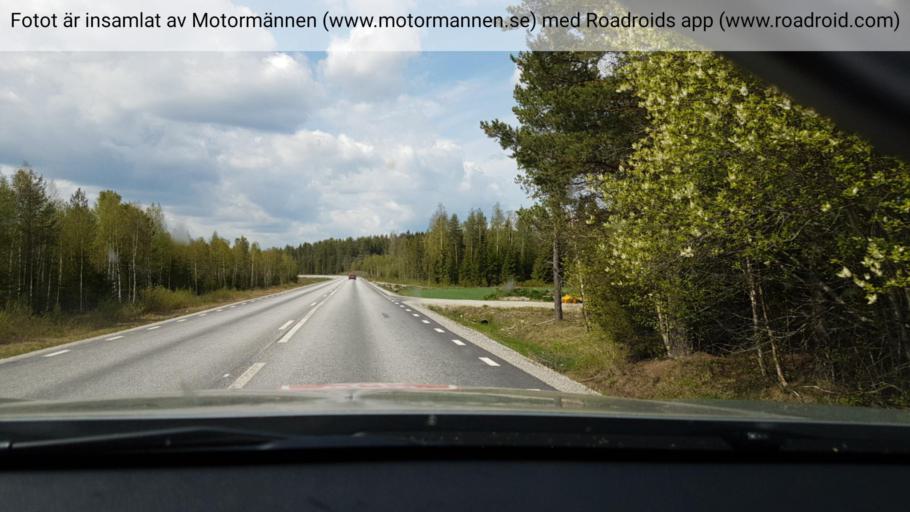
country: SE
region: Vaesterbotten
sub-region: Vindelns Kommun
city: Vindeln
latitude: 64.0499
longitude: 19.6756
